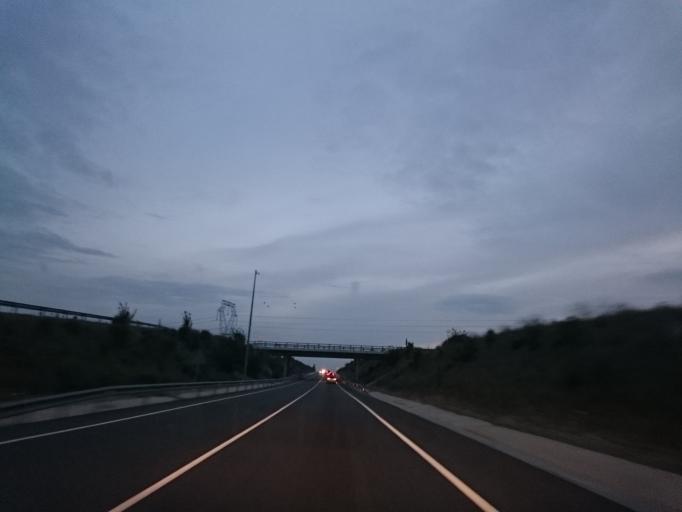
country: ES
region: Catalonia
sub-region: Provincia de Barcelona
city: La Granada
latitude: 41.3839
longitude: 1.7101
